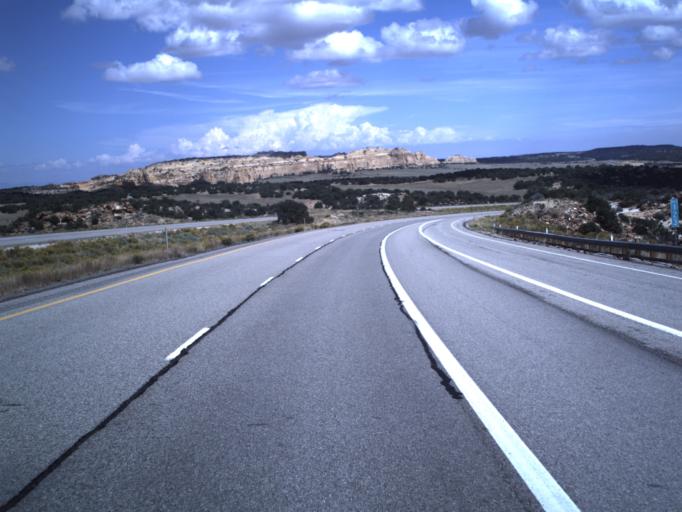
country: US
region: Utah
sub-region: Emery County
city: Ferron
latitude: 38.8652
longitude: -110.8095
